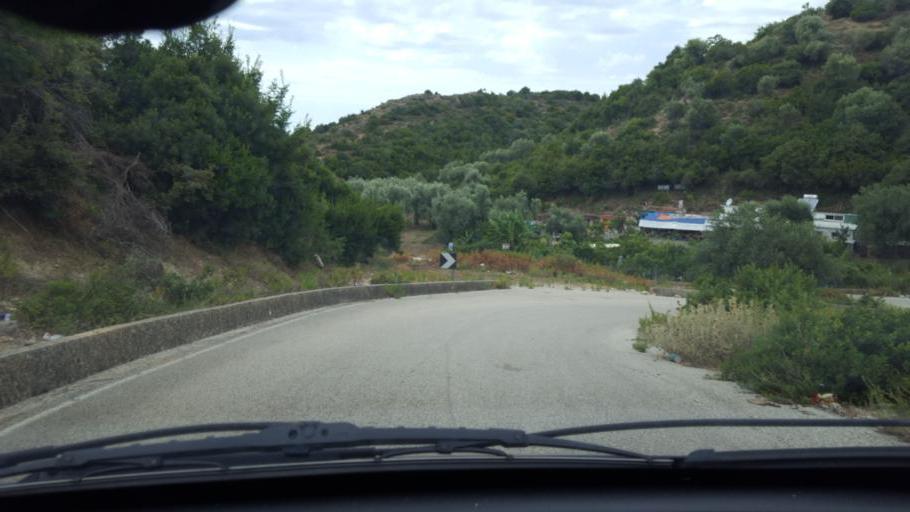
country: AL
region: Vlore
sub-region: Rrethi i Sarandes
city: Lukove
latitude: 39.9750
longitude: 19.9163
